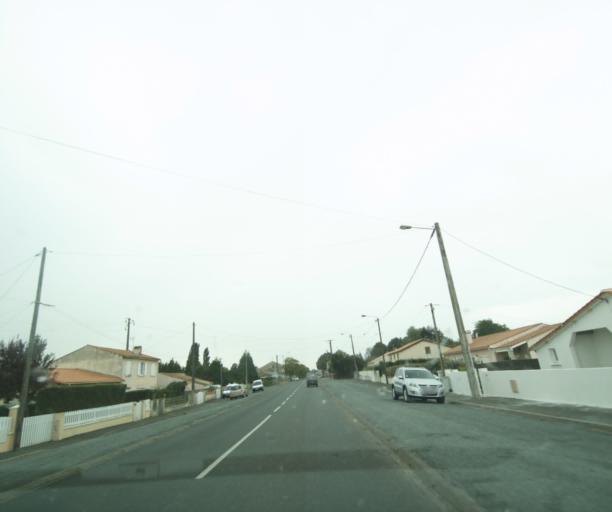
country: FR
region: Poitou-Charentes
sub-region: Departement de la Charente-Maritime
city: Breuil-Magne
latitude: 45.9522
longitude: -0.9398
